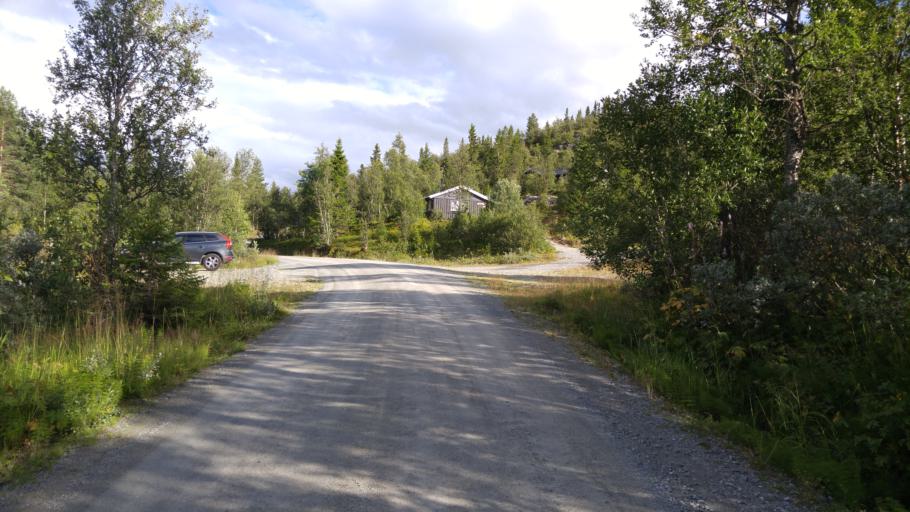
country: NO
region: Buskerud
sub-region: Hemsedal
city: Troim
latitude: 60.8486
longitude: 8.7127
